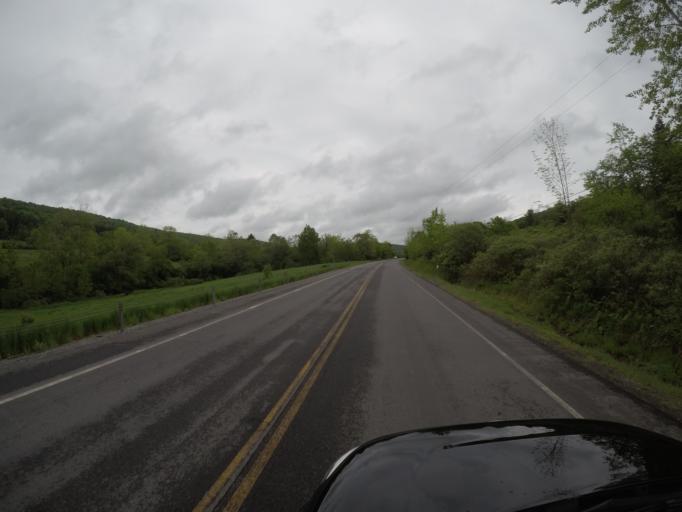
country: US
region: New York
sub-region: Delaware County
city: Delhi
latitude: 42.2048
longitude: -74.7926
